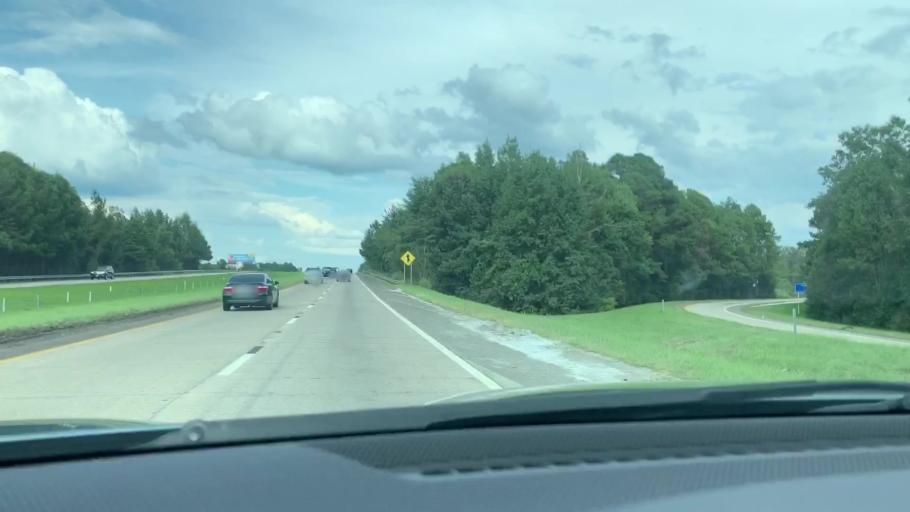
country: US
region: South Carolina
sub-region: Hampton County
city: Yemassee
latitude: 32.7012
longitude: -80.8731
